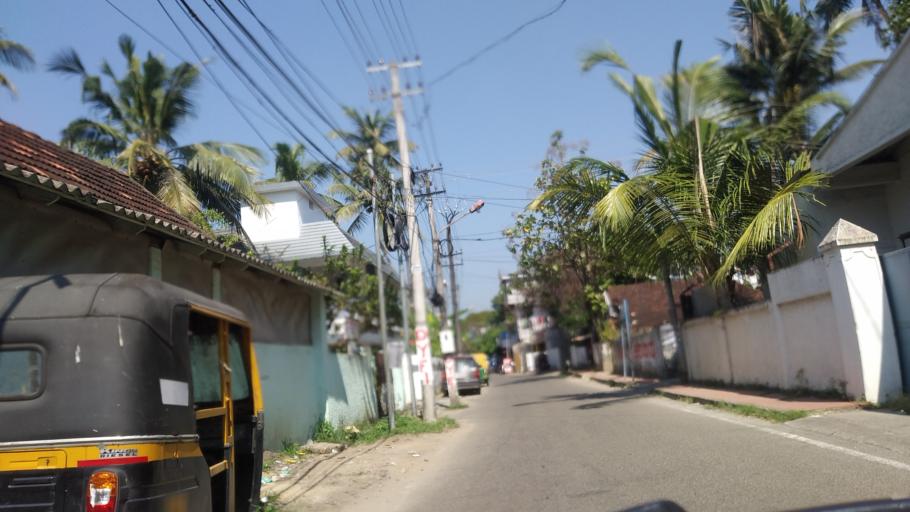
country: IN
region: Kerala
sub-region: Ernakulam
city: Cochin
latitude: 9.9425
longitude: 76.2478
